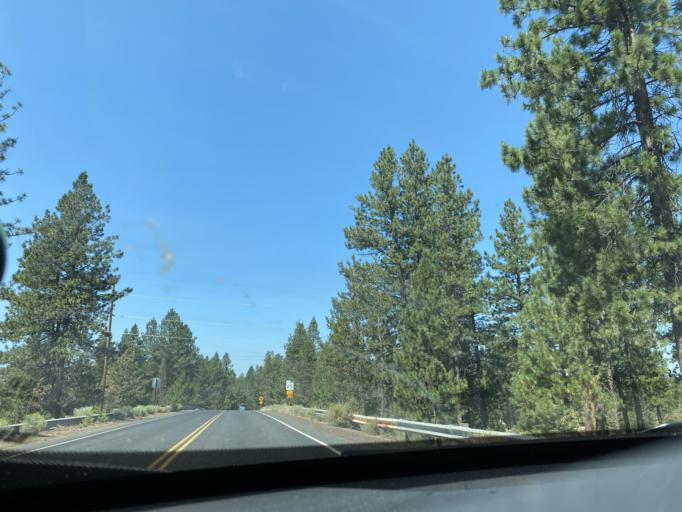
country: US
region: Oregon
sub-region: Deschutes County
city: Sunriver
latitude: 43.8935
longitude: -121.4144
